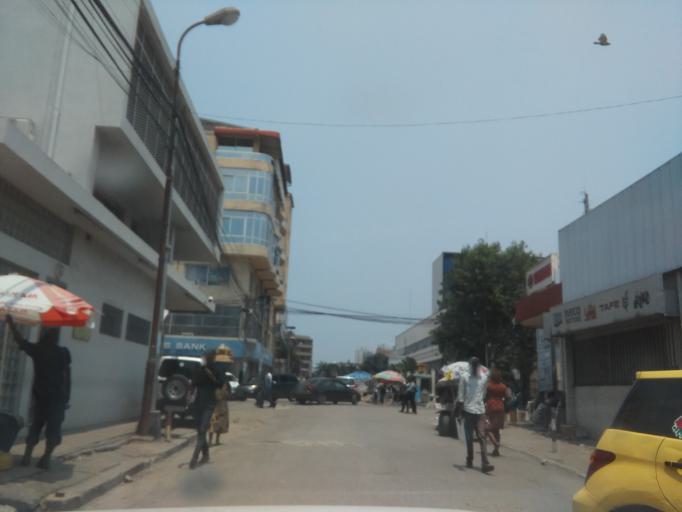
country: CD
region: Kinshasa
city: Kinshasa
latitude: -4.3048
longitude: 15.3088
